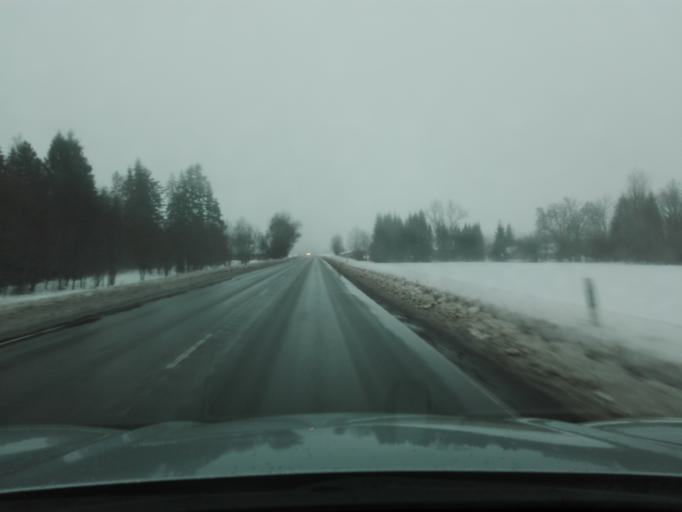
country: EE
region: Raplamaa
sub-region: Kohila vald
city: Kohila
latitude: 59.2039
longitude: 24.7816
